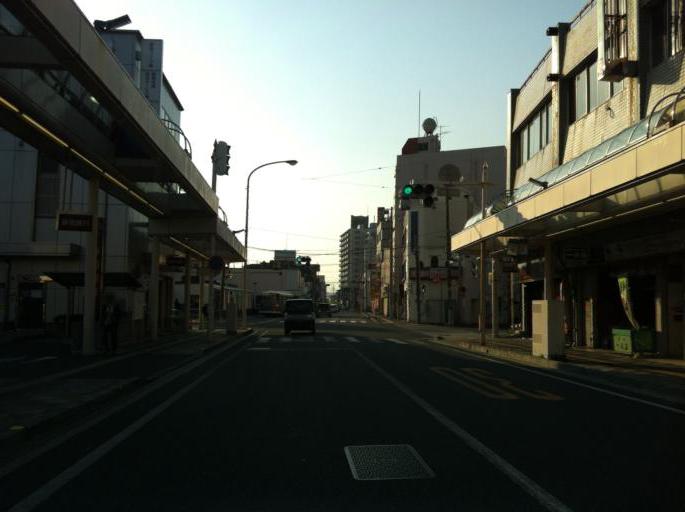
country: JP
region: Shizuoka
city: Fuji
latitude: 35.1633
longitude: 138.6846
